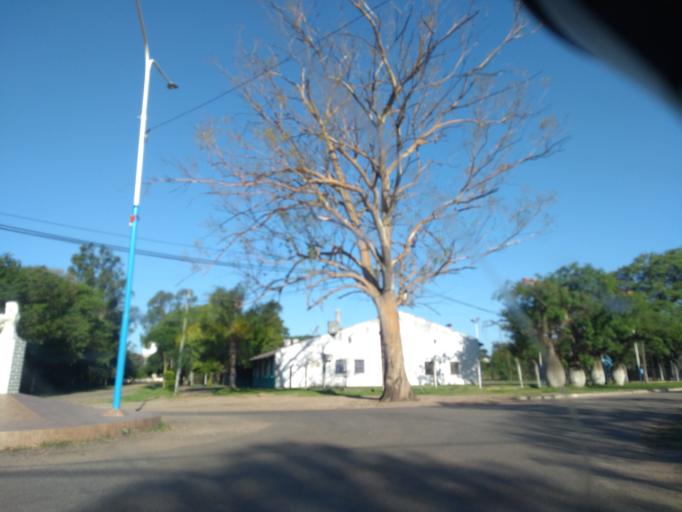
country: AR
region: Chaco
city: La Escondida
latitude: -27.1064
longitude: -59.4461
